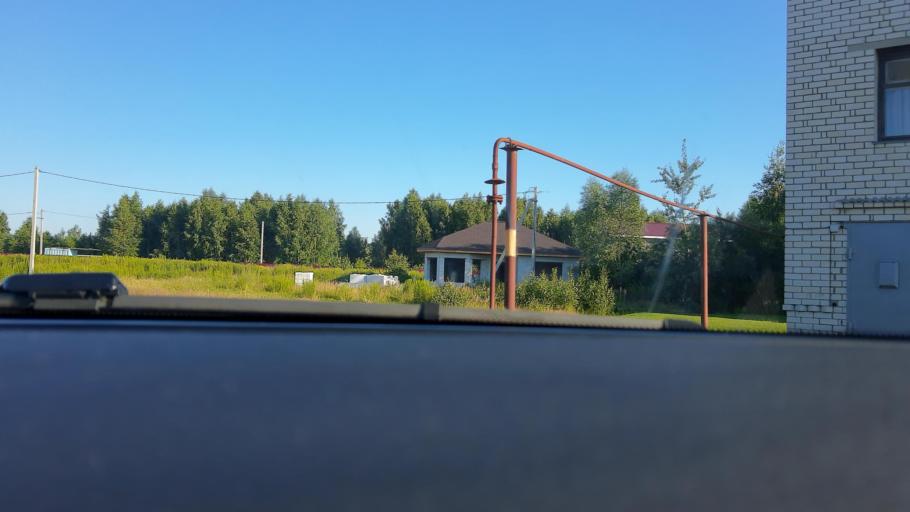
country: RU
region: Nizjnij Novgorod
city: Sitniki
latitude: 56.4054
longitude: 44.0369
